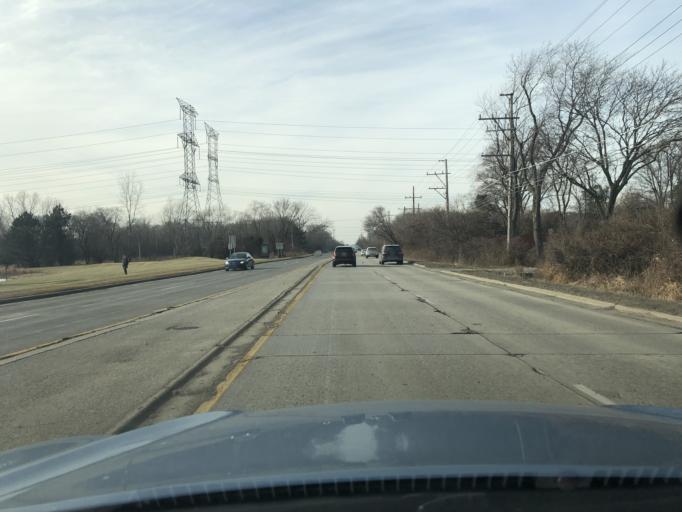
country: US
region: Illinois
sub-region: DuPage County
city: Itasca
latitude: 41.9928
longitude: -87.9919
